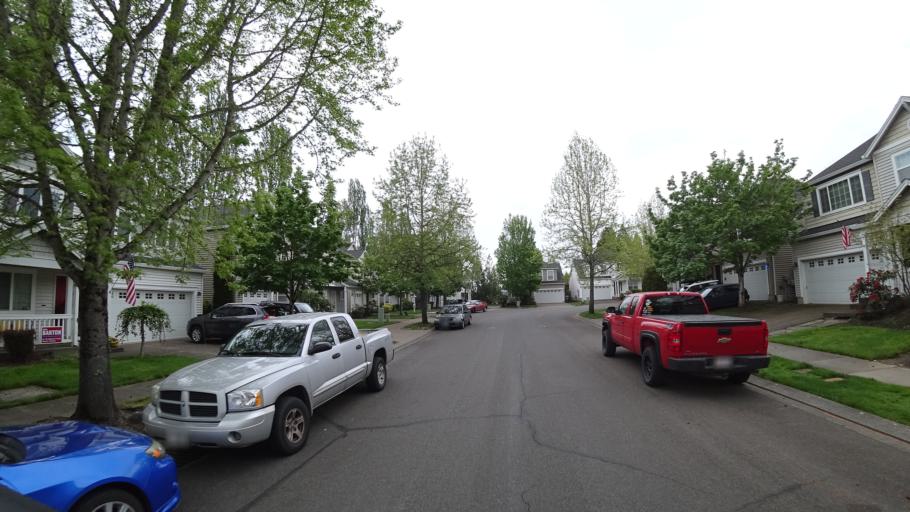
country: US
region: Oregon
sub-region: Washington County
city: Hillsboro
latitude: 45.5461
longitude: -122.9686
